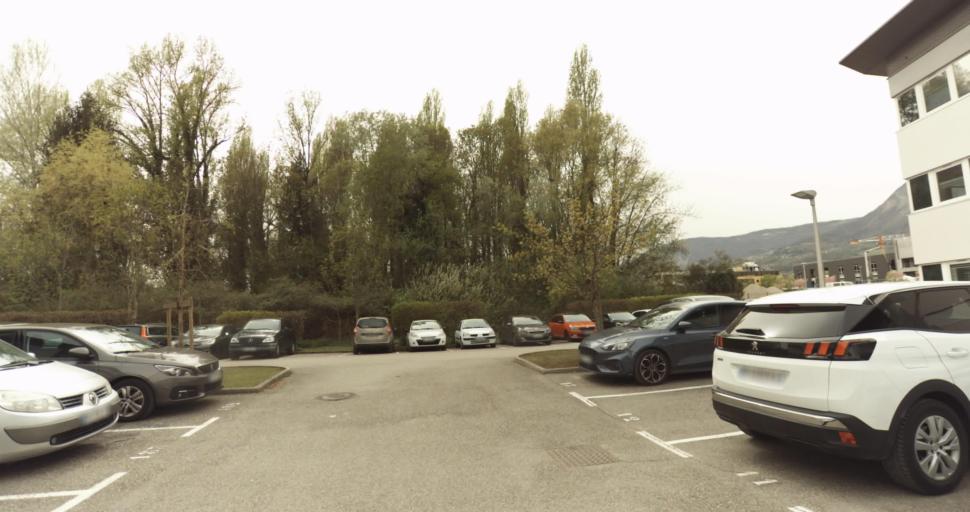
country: FR
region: Rhone-Alpes
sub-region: Departement de l'Isere
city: Montbonnot-Saint-Martin
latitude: 45.2164
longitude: 5.8140
